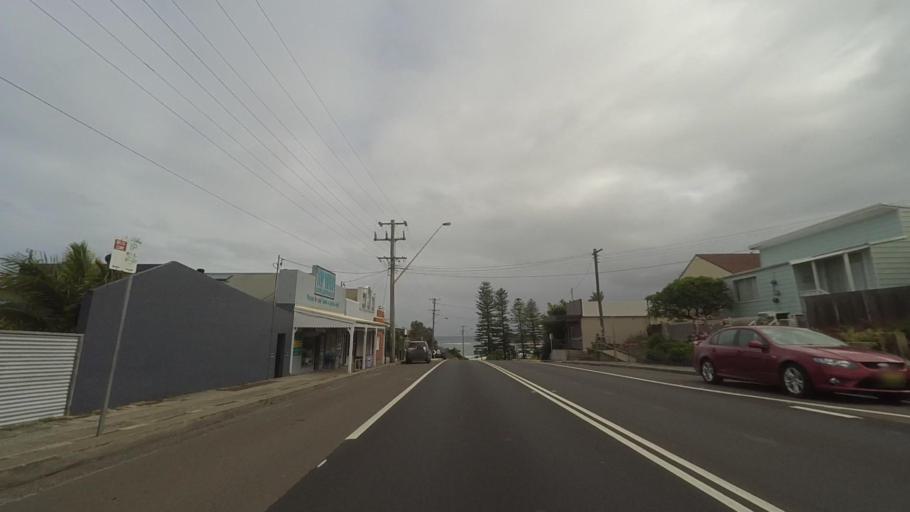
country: AU
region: New South Wales
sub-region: Wollongong
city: Bulli
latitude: -34.2920
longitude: 150.9444
